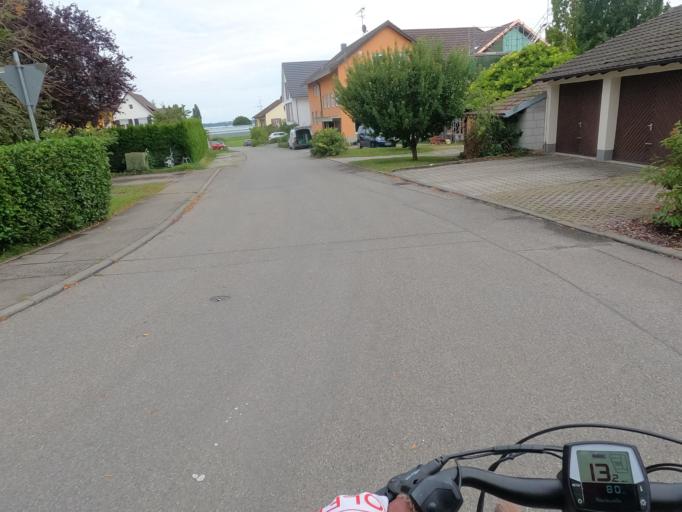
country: DE
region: Baden-Wuerttemberg
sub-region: Freiburg Region
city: Reichenau
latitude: 47.6856
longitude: 9.0769
